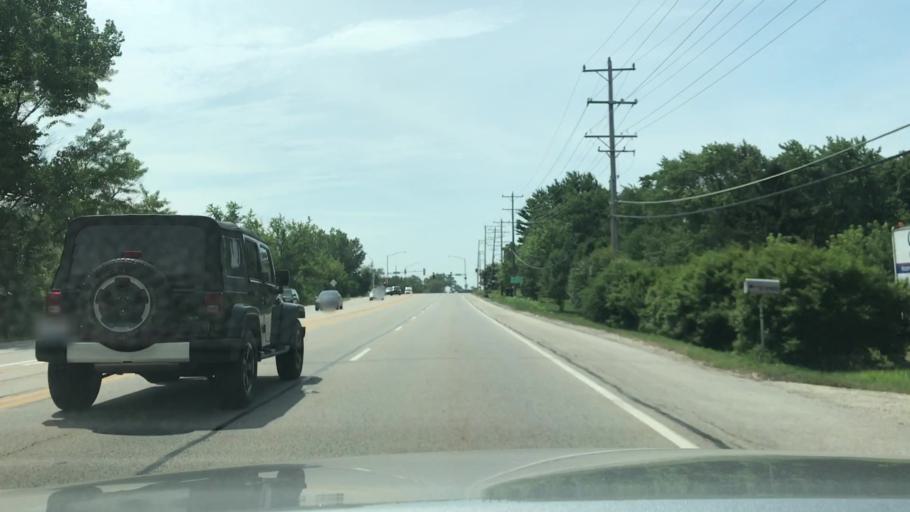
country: US
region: Illinois
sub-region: DuPage County
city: Darien
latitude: 41.7257
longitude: -88.0096
